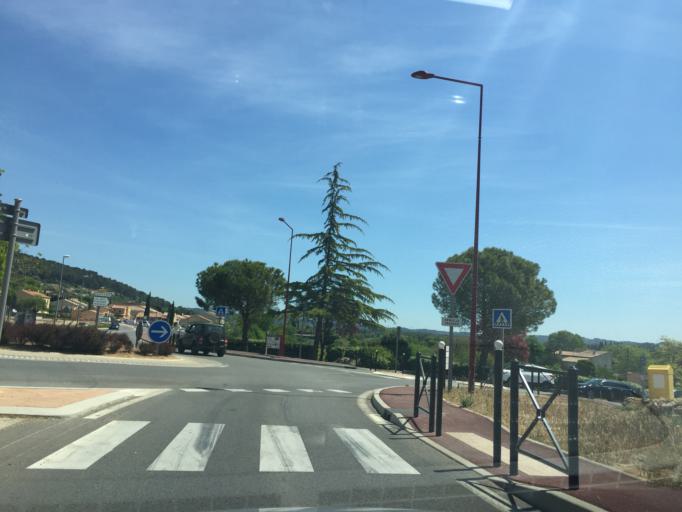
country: FR
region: Provence-Alpes-Cote d'Azur
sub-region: Departement du Var
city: Lorgues
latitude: 43.4896
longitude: 6.3581
